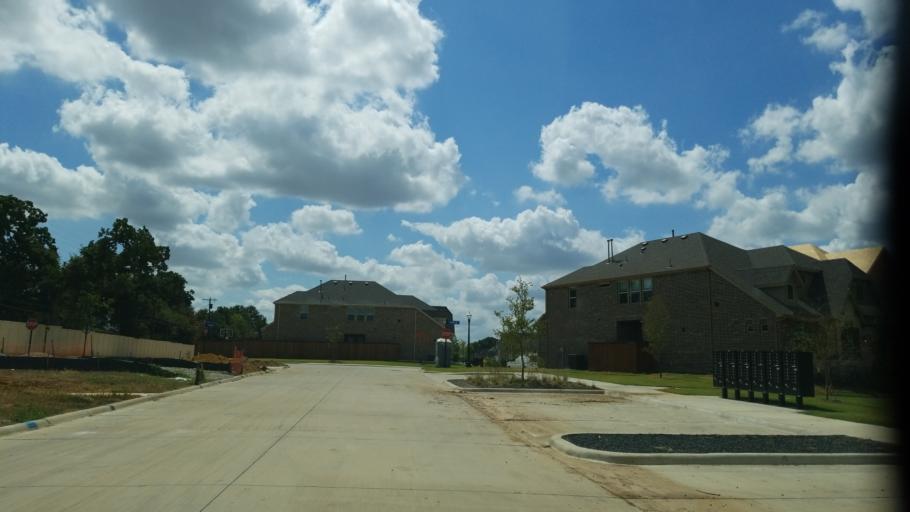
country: US
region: Texas
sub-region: Tarrant County
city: Euless
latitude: 32.8350
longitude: -97.0944
